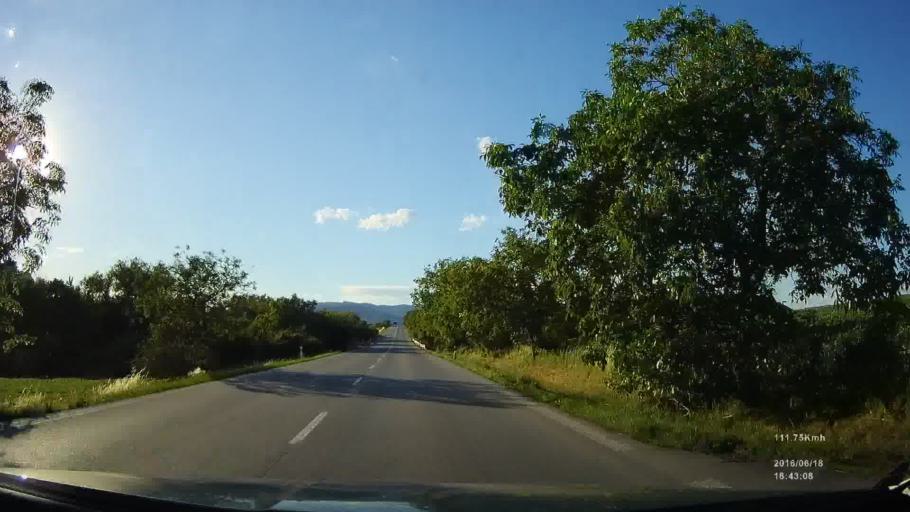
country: SK
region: Kosicky
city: Secovce
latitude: 48.7143
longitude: 21.6157
